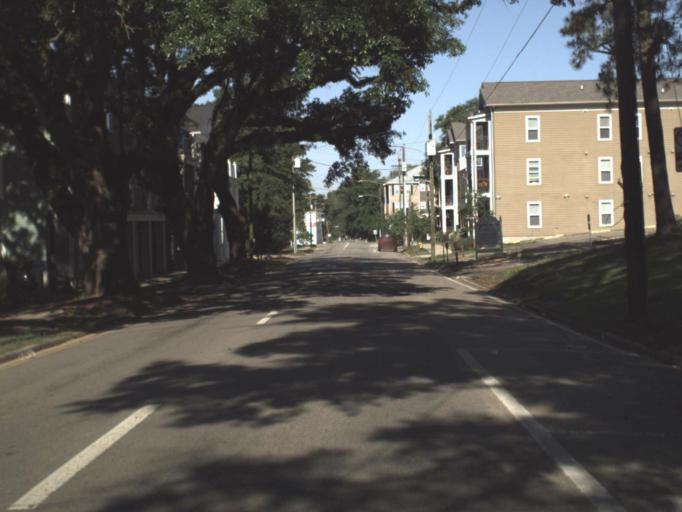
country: US
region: Florida
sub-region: Leon County
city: Tallahassee
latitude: 30.4388
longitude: -84.2945
